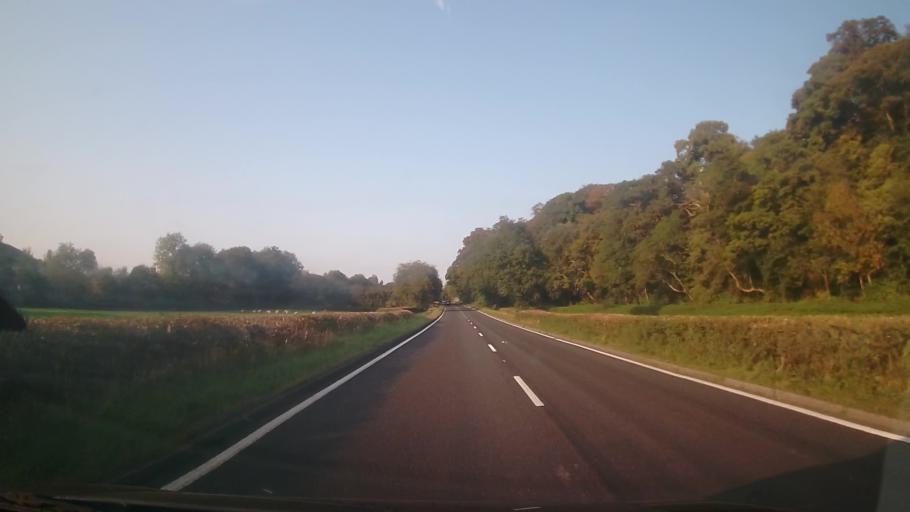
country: GB
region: Wales
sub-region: Sir Powys
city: Mochdre
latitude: 52.4906
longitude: -3.4341
